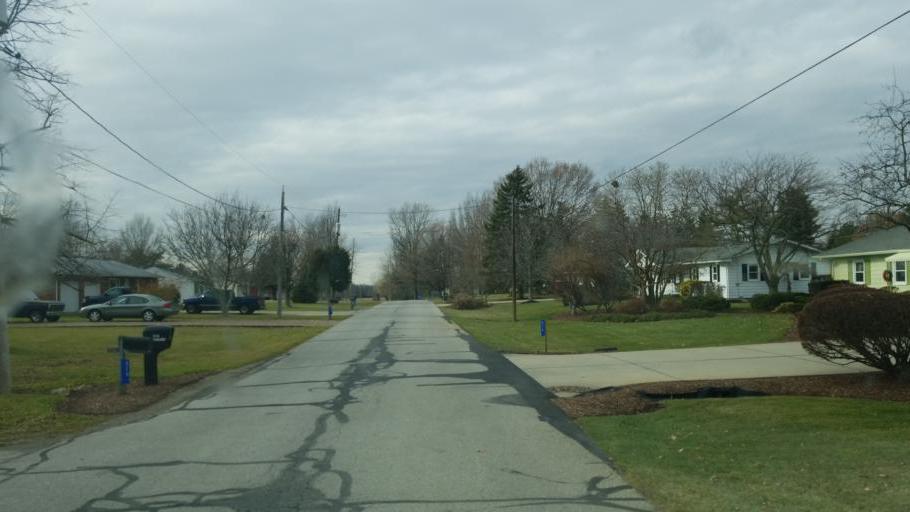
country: US
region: Ohio
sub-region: Crawford County
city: Galion
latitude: 40.7585
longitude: -82.7797
